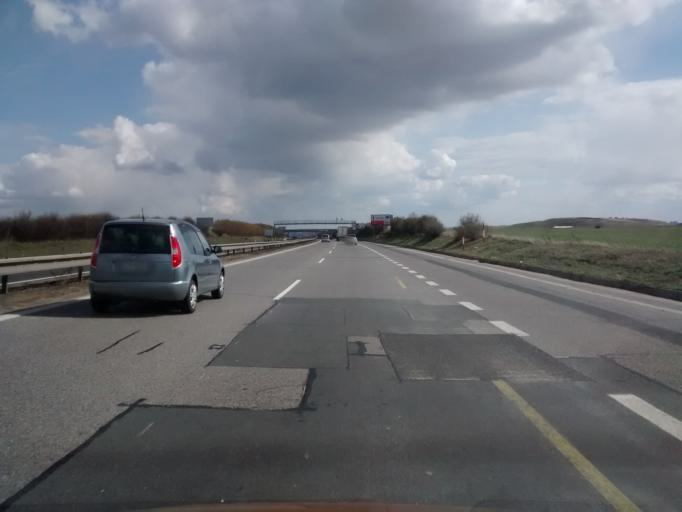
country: CZ
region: Central Bohemia
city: Zdiby
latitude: 50.1687
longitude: 14.4624
